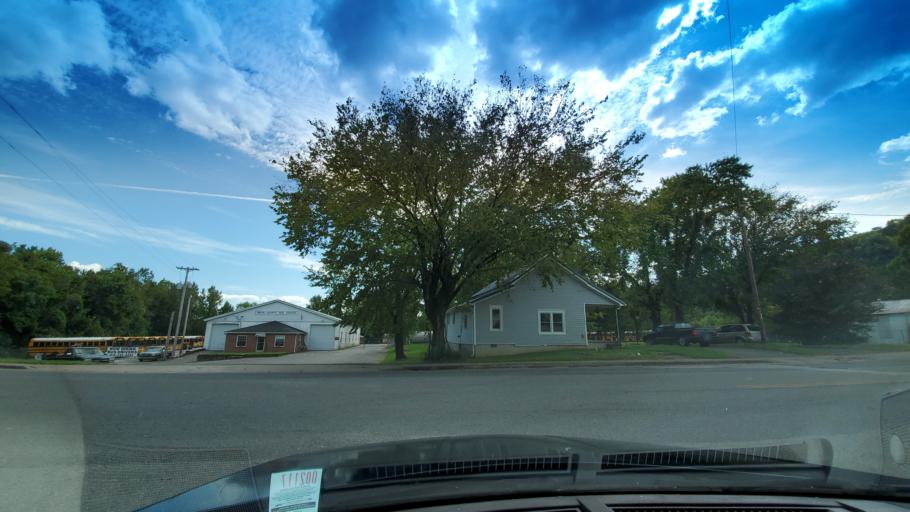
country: US
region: Tennessee
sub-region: Smith County
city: Carthage
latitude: 36.2483
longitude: -85.9514
